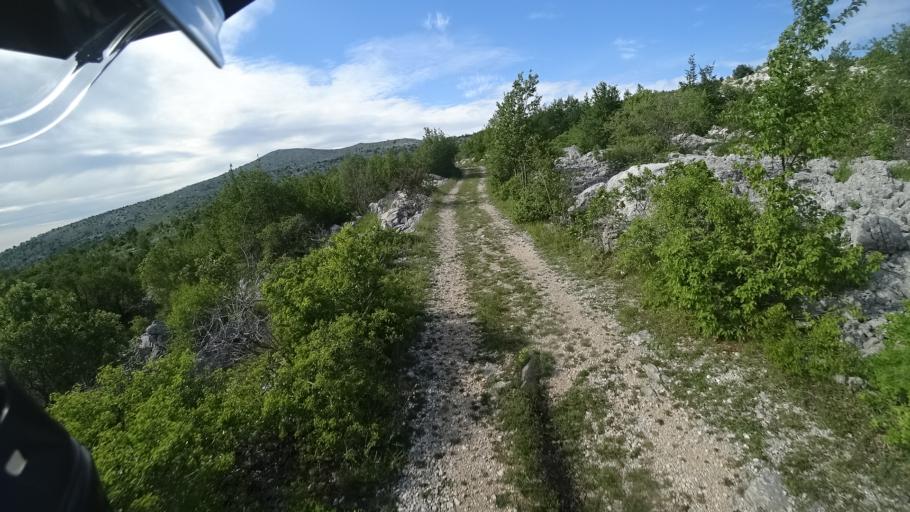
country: HR
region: Splitsko-Dalmatinska
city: Hrvace
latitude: 43.7932
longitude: 16.4345
